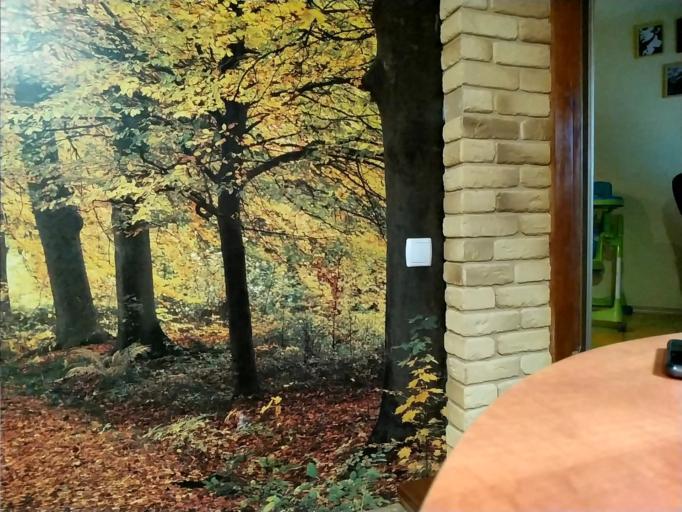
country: BY
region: Minsk
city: Il'ya
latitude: 54.4242
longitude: 27.5207
